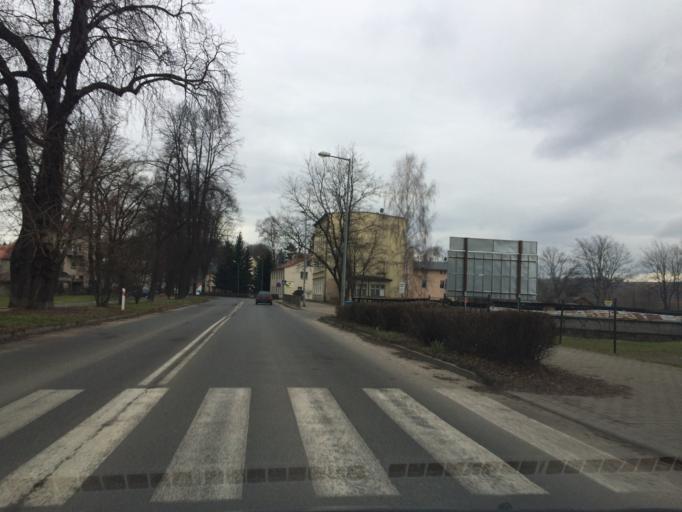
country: PL
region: Lower Silesian Voivodeship
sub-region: Powiat lwowecki
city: Lwowek Slaski
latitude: 51.1112
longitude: 15.5902
